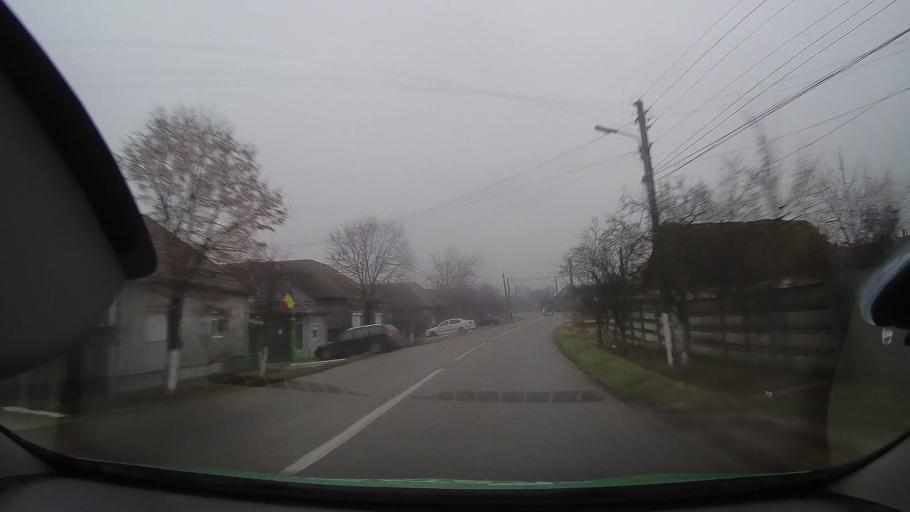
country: RO
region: Bihor
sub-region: Comuna Tulca
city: Tulca
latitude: 46.7871
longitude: 21.7825
